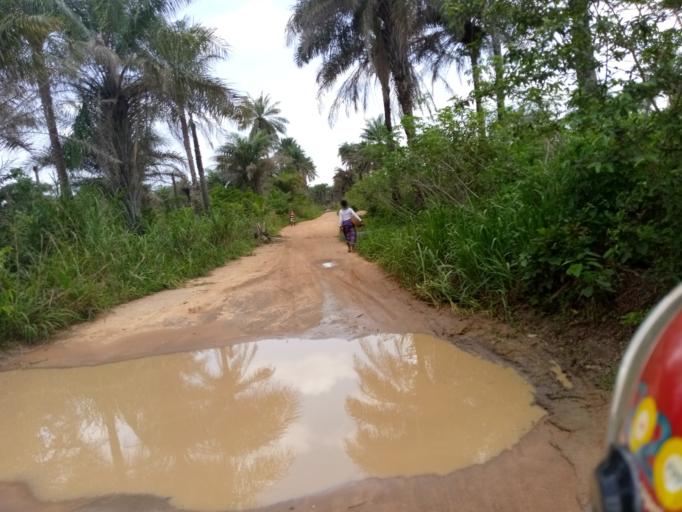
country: SL
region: Western Area
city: Waterloo
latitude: 8.3970
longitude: -12.9936
